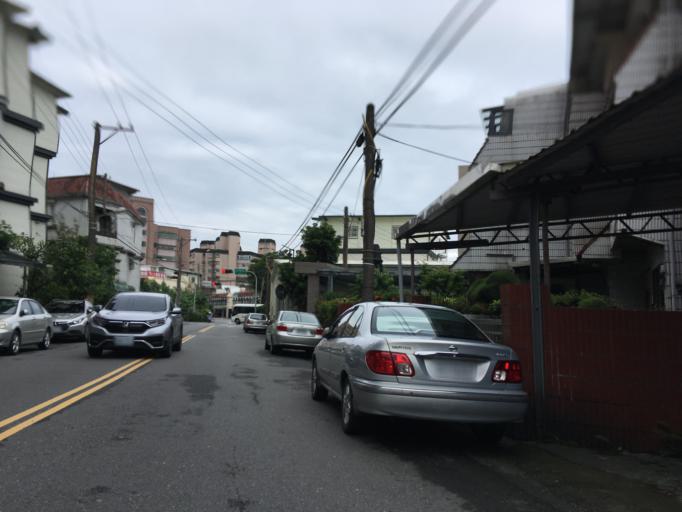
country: TW
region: Taiwan
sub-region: Yilan
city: Yilan
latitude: 24.7428
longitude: 121.7526
